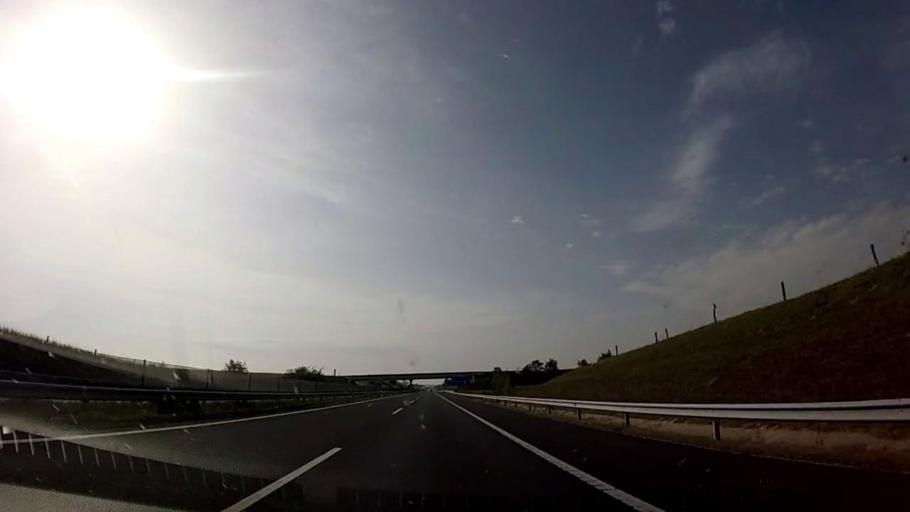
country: HU
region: Zala
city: Nagykanizsa
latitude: 46.4696
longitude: 16.8968
